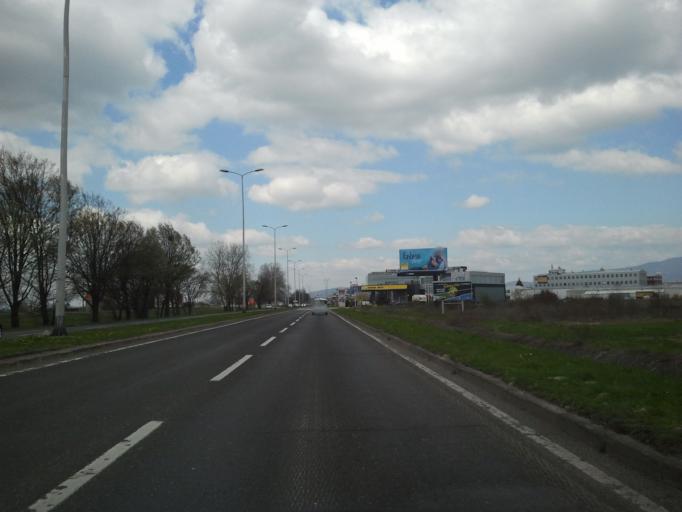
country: HR
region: Grad Zagreb
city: Odra
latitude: 45.7409
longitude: 16.0027
